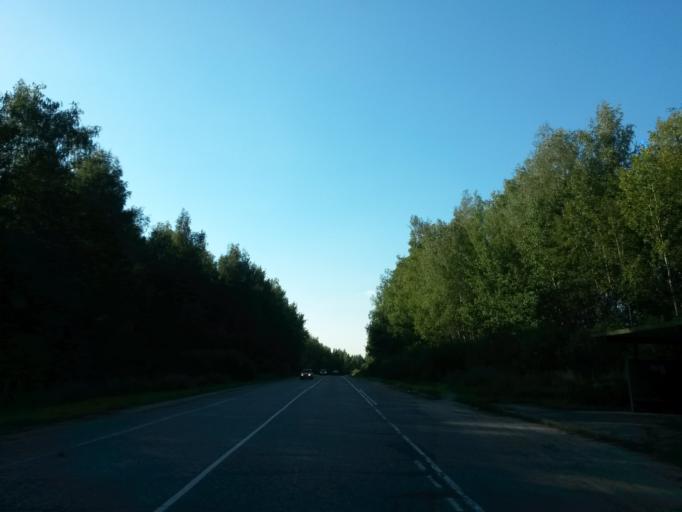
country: RU
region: Ivanovo
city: Pistsovo
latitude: 57.0893
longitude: 40.6667
